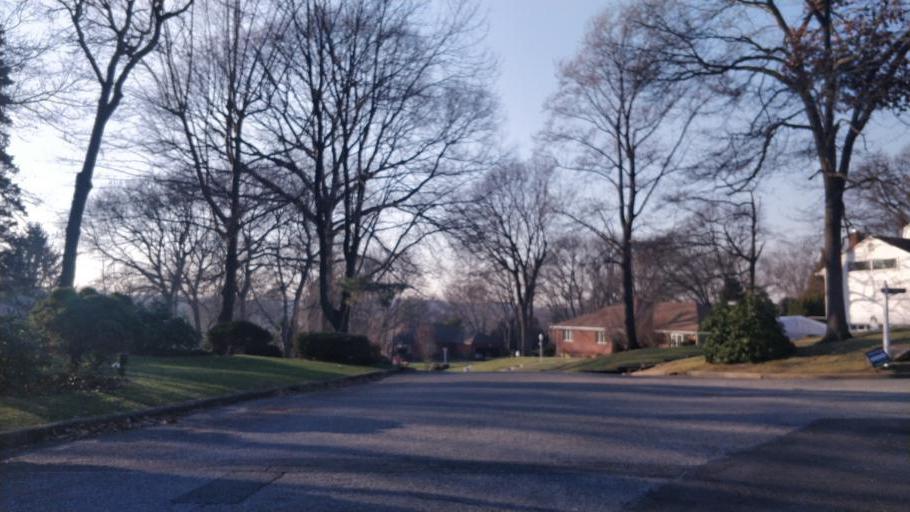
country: US
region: New York
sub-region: Nassau County
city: Bayville
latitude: 40.9023
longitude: -73.5672
